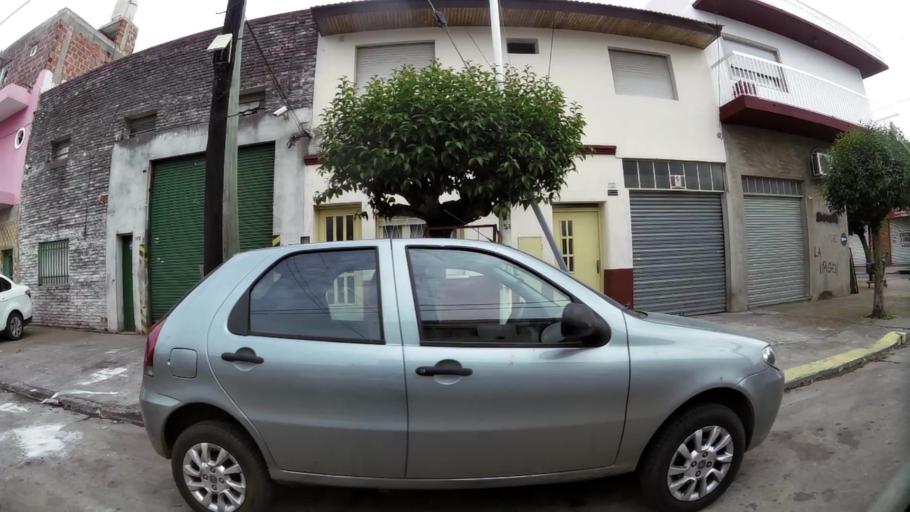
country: AR
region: Buenos Aires F.D.
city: Villa Lugano
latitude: -34.6820
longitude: -58.5072
